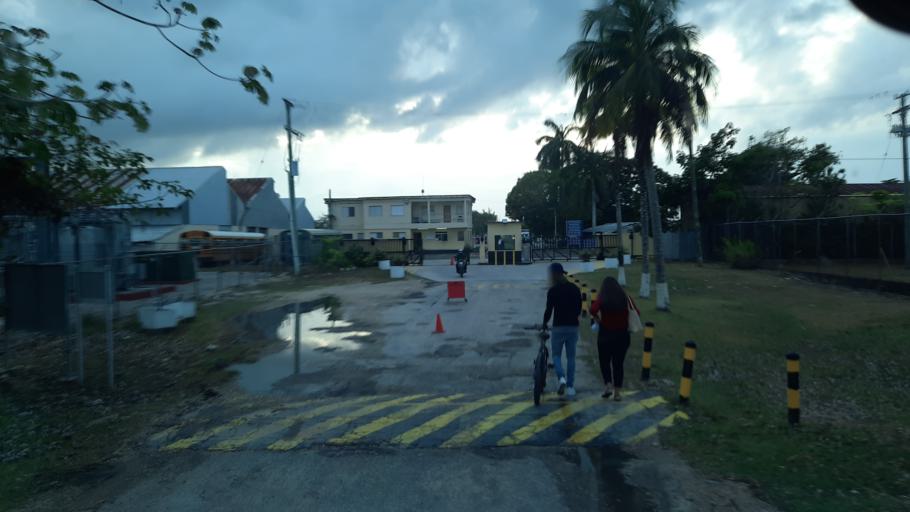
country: BZ
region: Belize
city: Belize City
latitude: 17.5427
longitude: -88.3029
